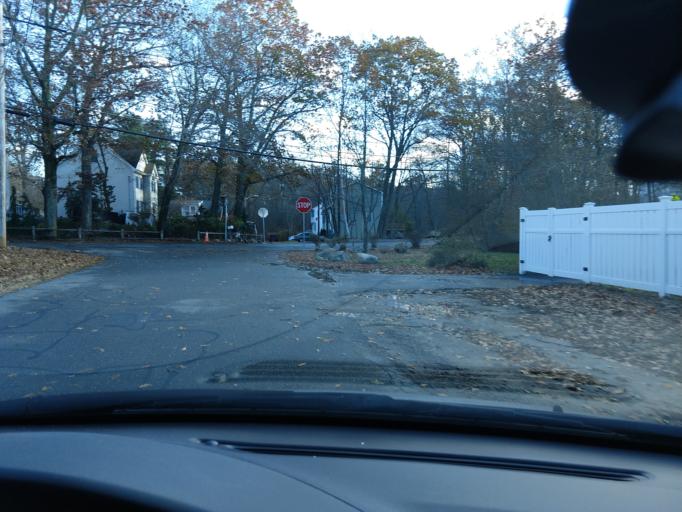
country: US
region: Massachusetts
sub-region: Middlesex County
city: Billerica
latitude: 42.5339
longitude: -71.2676
